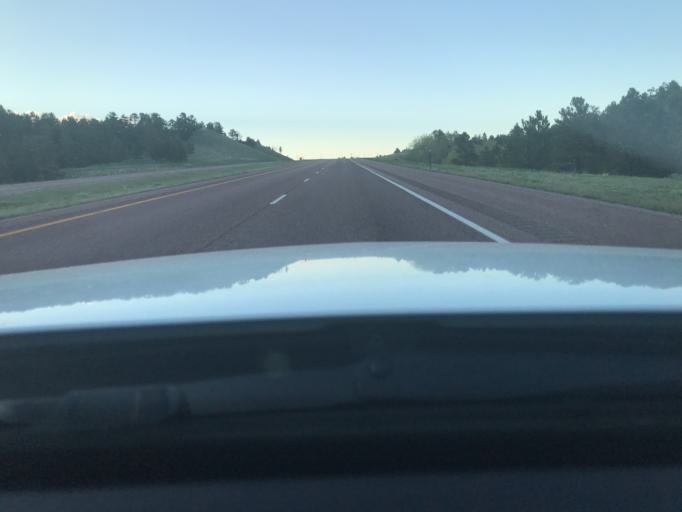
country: US
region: Wyoming
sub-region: Platte County
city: Guernsey
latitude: 42.4325
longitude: -105.0353
